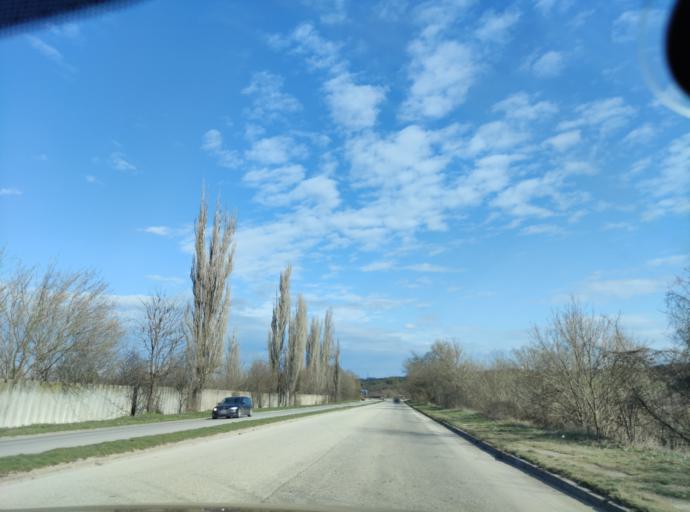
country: BG
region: Pleven
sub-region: Obshtina Dolna Mitropoliya
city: Dolna Mitropoliya
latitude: 43.4331
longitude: 24.5425
